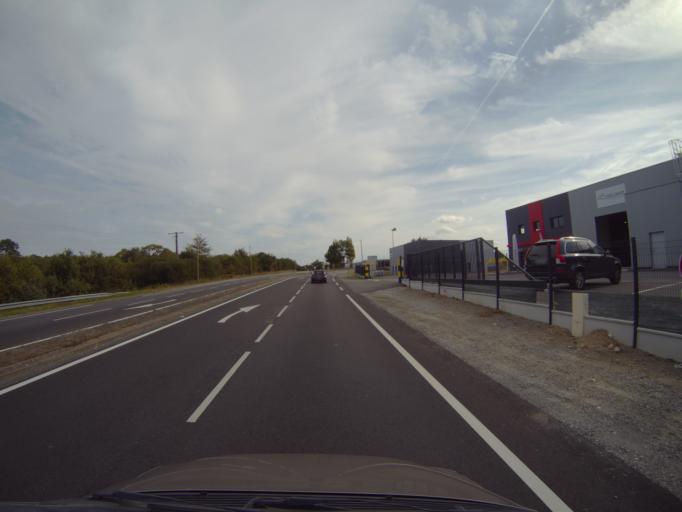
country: FR
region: Pays de la Loire
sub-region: Departement de la Loire-Atlantique
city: Sautron
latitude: 47.2440
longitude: -1.6689
